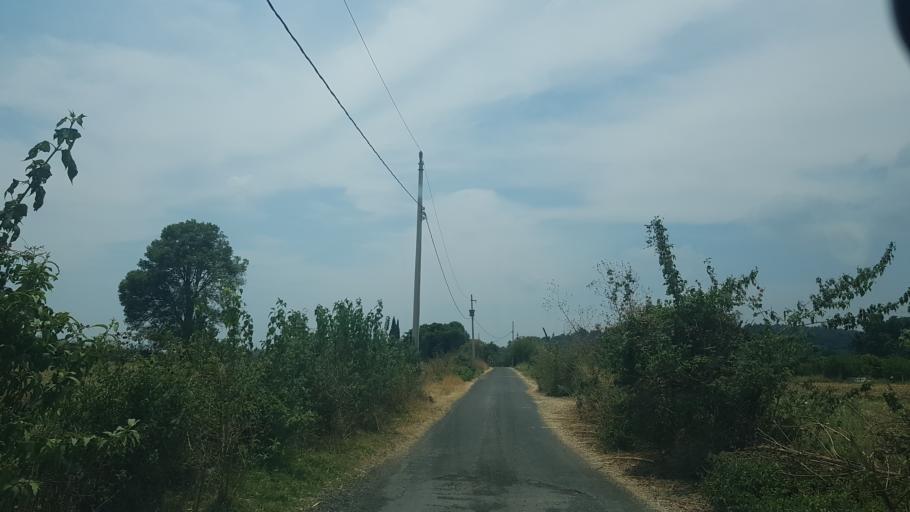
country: MX
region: Puebla
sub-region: Atzitzihuacan
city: Santiago Atzitzihuacan
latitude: 18.8622
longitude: -98.6111
